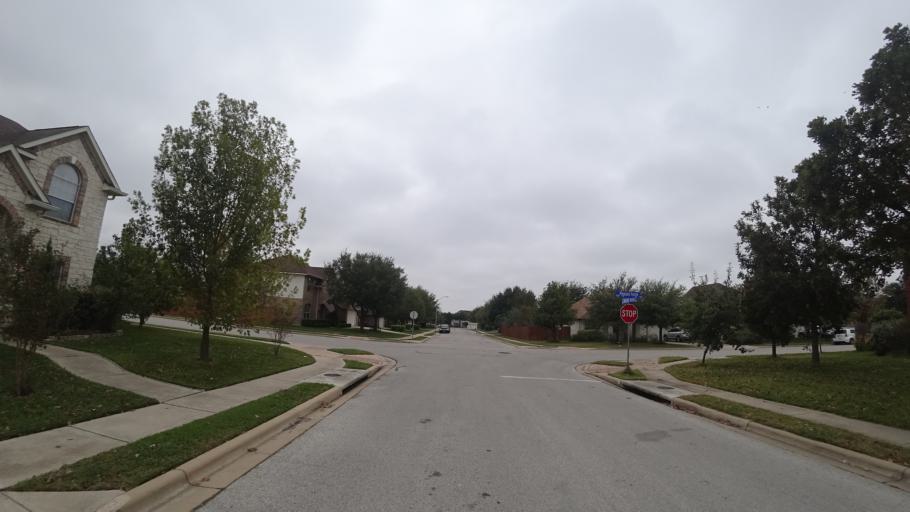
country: US
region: Texas
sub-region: Travis County
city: Pflugerville
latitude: 30.4270
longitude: -97.6163
